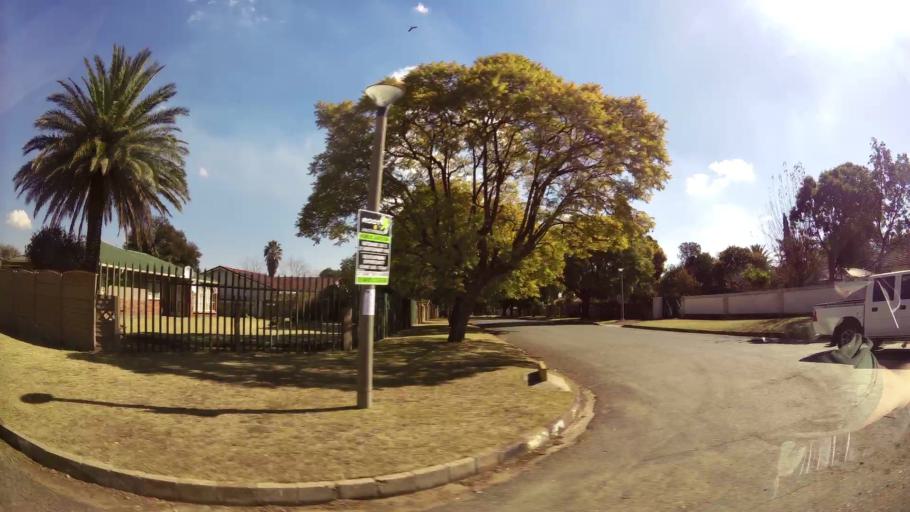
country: ZA
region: Mpumalanga
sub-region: Nkangala District Municipality
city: Witbank
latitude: -25.8833
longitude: 29.2256
